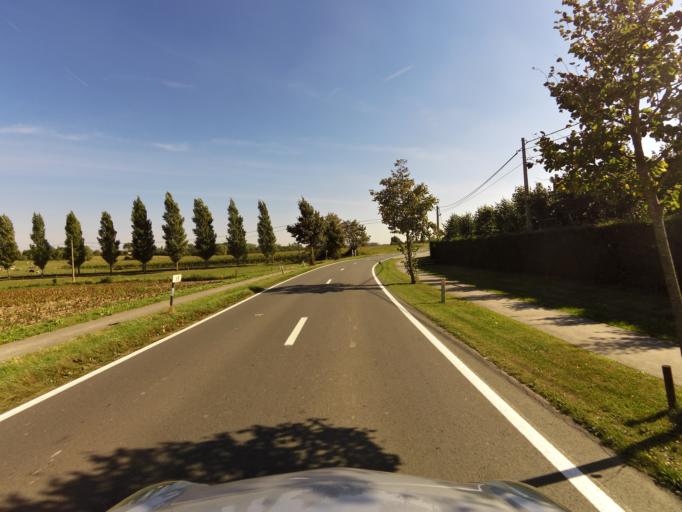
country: BE
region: Flanders
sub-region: Provincie West-Vlaanderen
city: Poperinge
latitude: 50.9166
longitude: 2.7340
